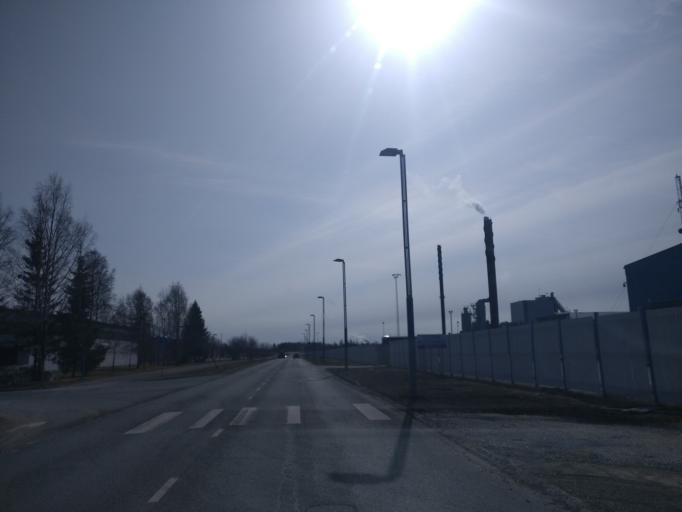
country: FI
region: Lapland
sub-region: Kemi-Tornio
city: Kemi
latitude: 65.7359
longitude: 24.5820
